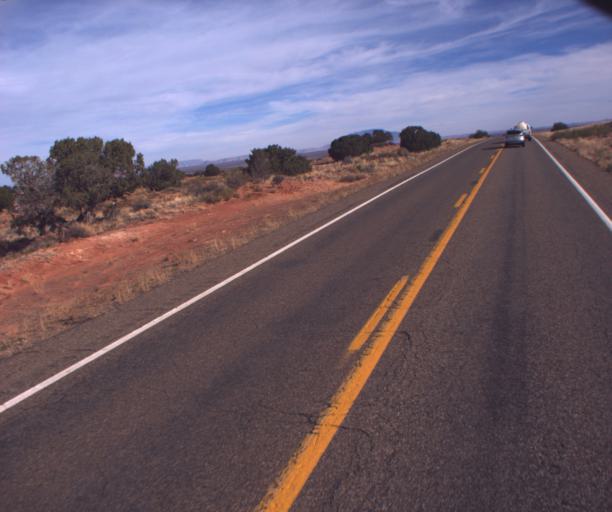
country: US
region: Arizona
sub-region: Coconino County
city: Kaibito
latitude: 36.5889
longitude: -111.1014
